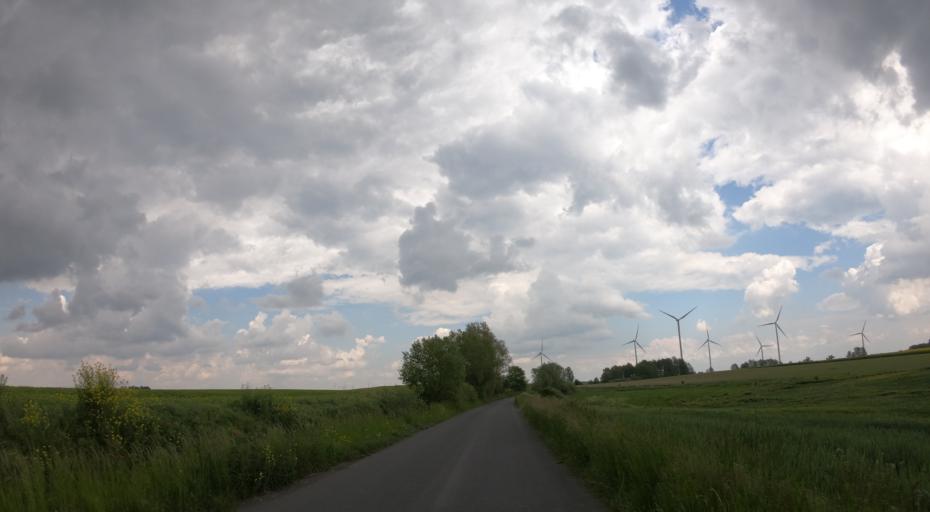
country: PL
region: West Pomeranian Voivodeship
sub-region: Powiat pyrzycki
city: Kozielice
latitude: 53.1415
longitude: 14.7632
